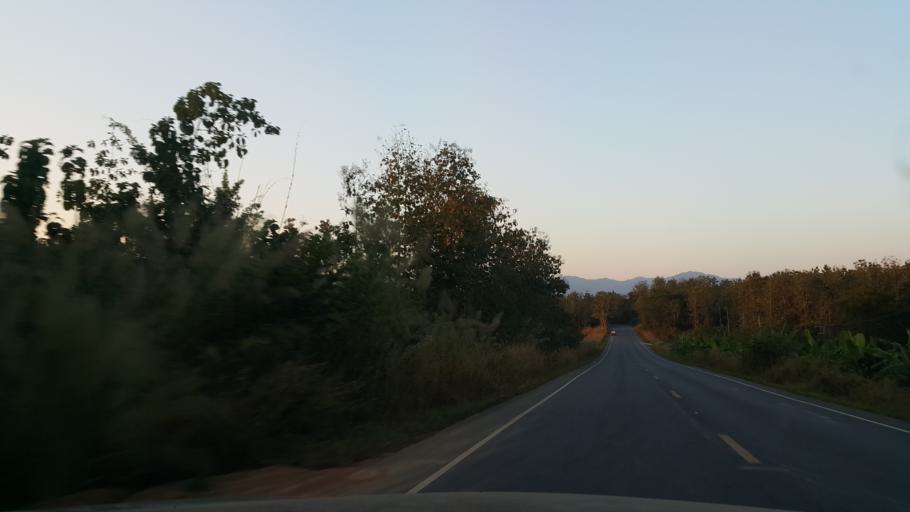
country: TH
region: Phrae
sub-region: Amphoe Wang Chin
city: Wang Chin
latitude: 17.8556
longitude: 99.6272
